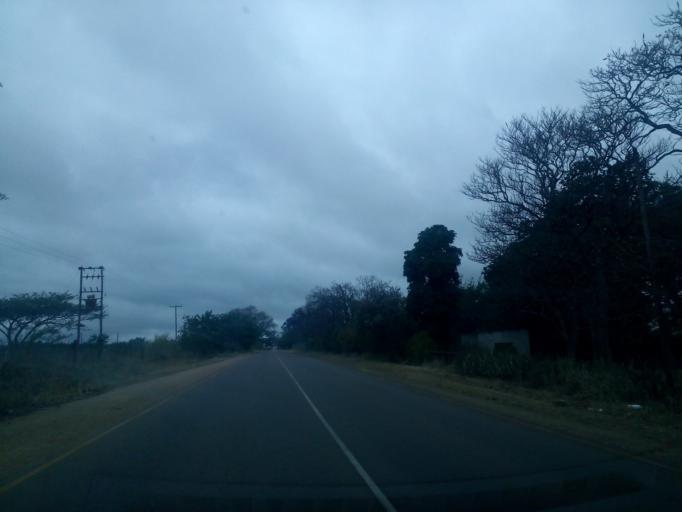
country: ZA
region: Limpopo
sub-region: Vhembe District Municipality
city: Louis Trichardt
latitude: -23.0788
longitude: 29.9024
